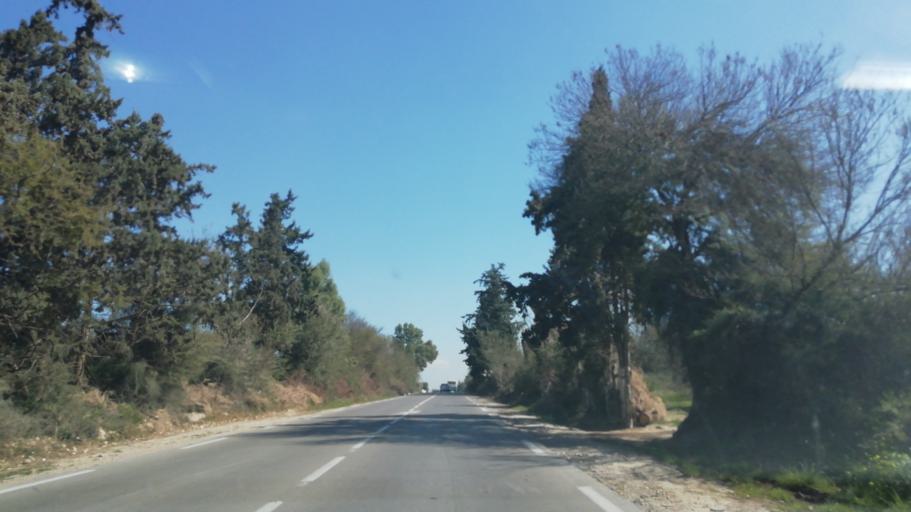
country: DZ
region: Mascara
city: Sig
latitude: 35.5760
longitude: -0.0032
